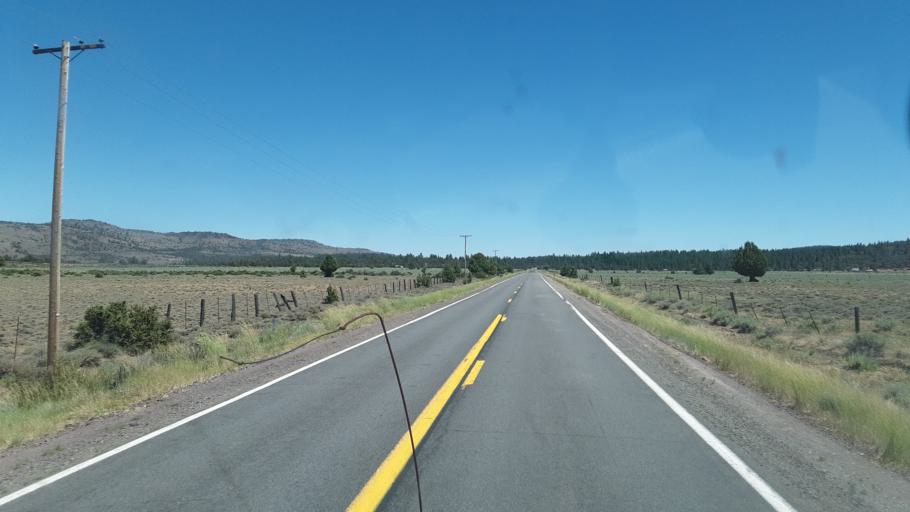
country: US
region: California
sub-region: Lassen County
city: Susanville
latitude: 40.5270
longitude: -120.5977
